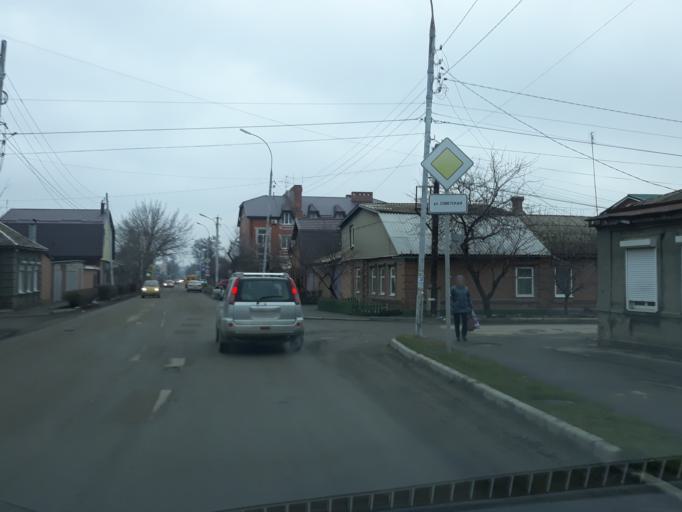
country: RU
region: Rostov
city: Taganrog
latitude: 47.2238
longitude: 38.9237
